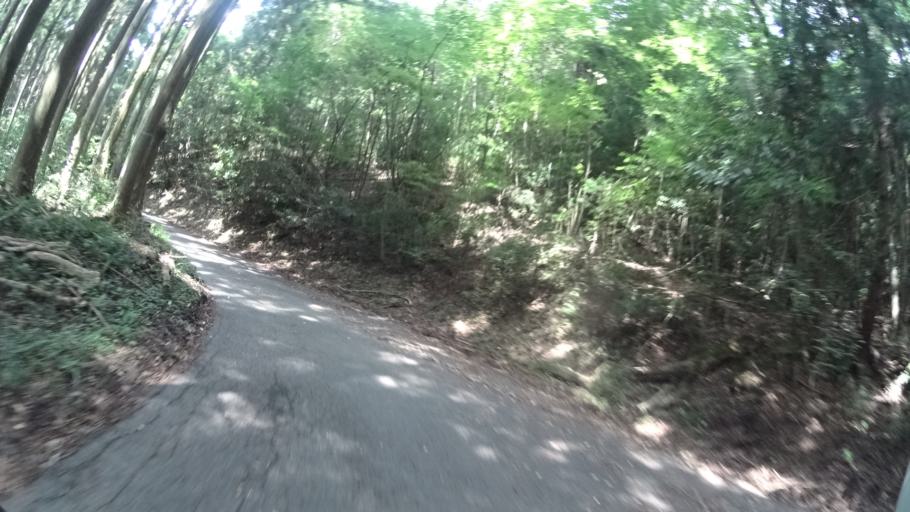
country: JP
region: Yamaguchi
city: Hagi
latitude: 34.4935
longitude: 131.5659
